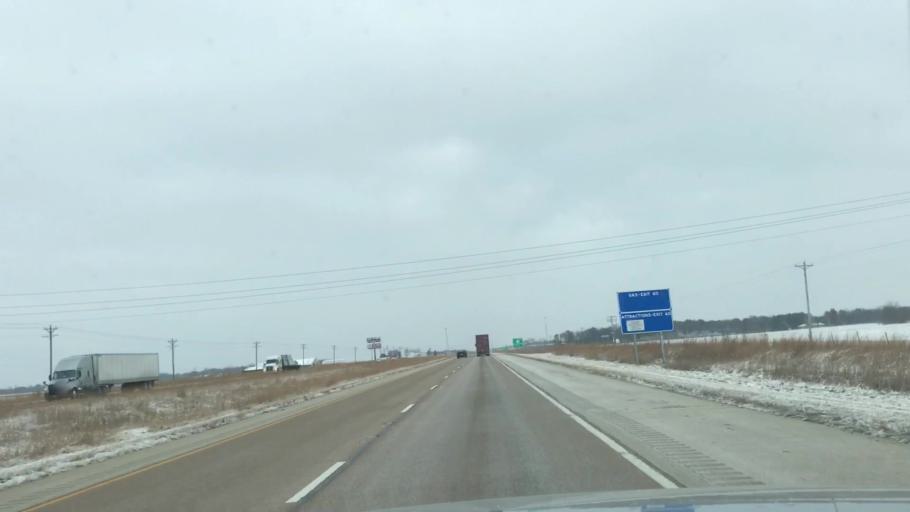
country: US
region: Illinois
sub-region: Montgomery County
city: Litchfield
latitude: 39.2563
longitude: -89.6411
